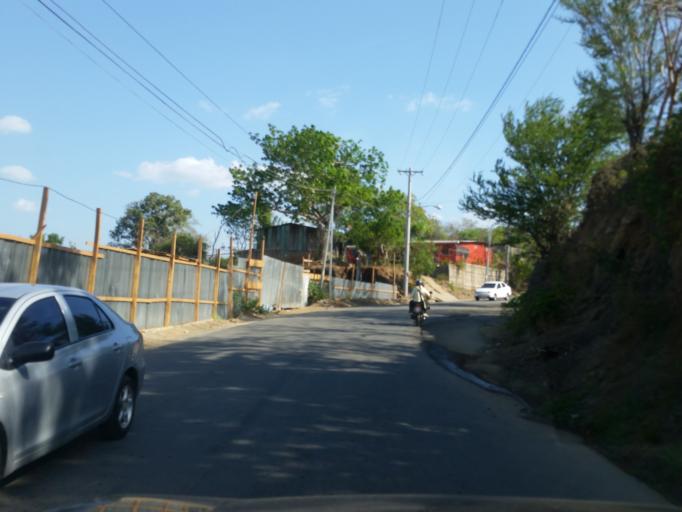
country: NI
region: Managua
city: Managua
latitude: 12.0990
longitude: -86.2912
